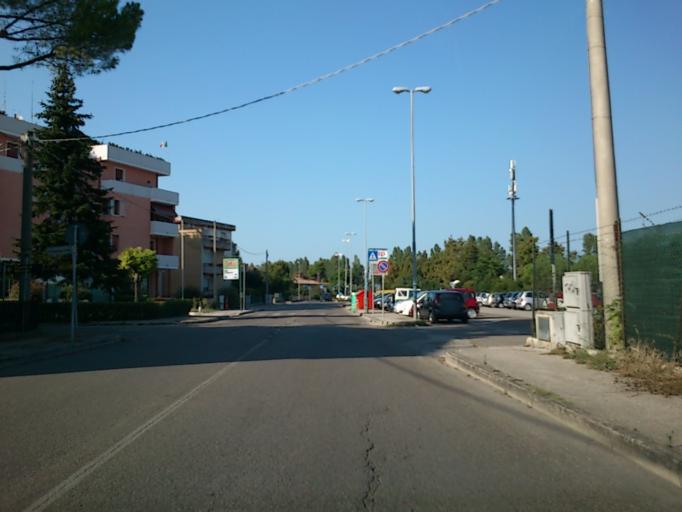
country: IT
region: The Marches
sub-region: Provincia di Pesaro e Urbino
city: Fano
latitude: 43.8302
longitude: 13.0126
